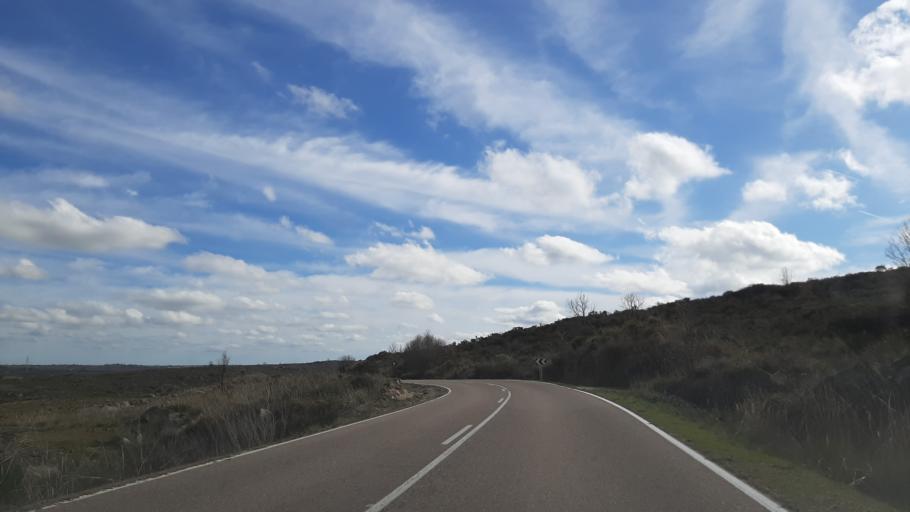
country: ES
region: Castille and Leon
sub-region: Provincia de Salamanca
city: Villarino de los Aires
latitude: 41.2599
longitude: -6.4252
